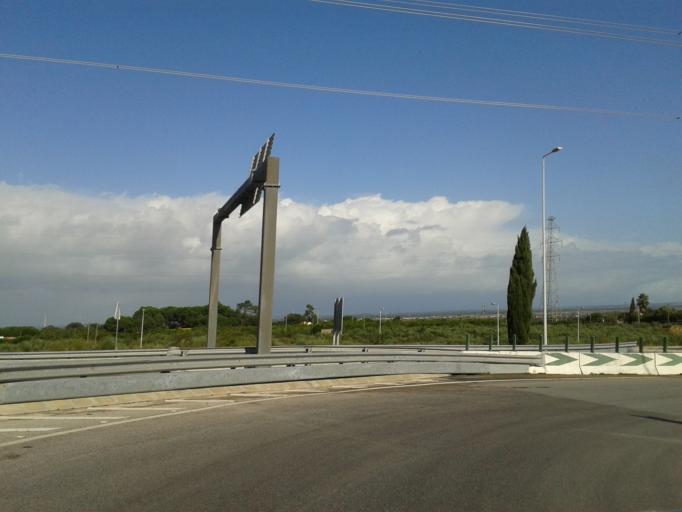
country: PT
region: Setubal
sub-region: Palmela
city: Palmela
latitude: 38.5847
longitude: -8.8900
